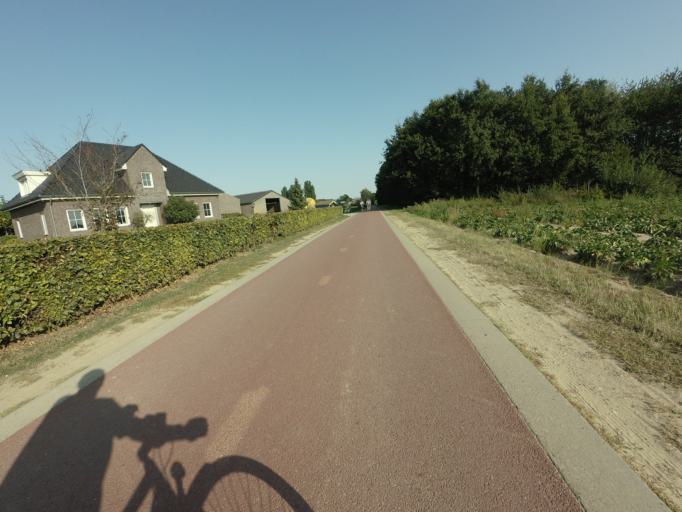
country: NL
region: Limburg
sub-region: Gemeente Roerdalen
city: Montfort
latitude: 51.1513
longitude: 5.9584
